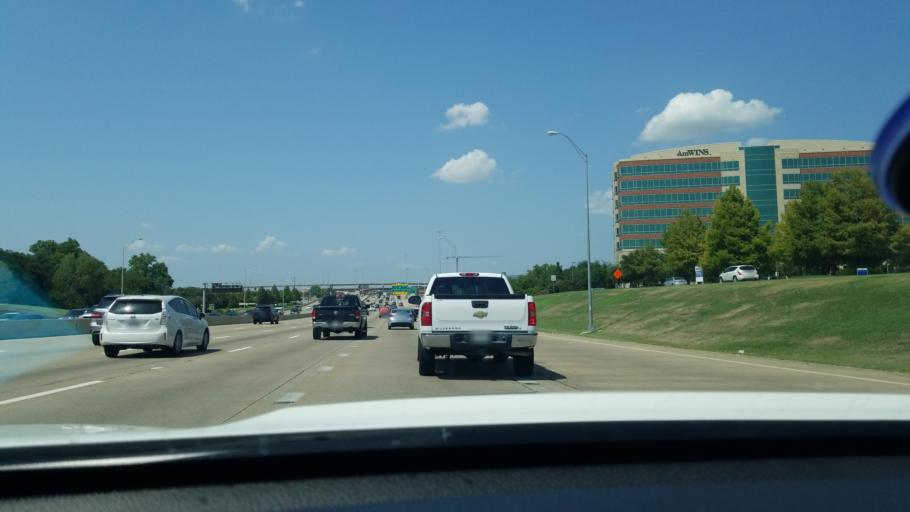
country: US
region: Texas
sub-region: Collin County
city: Plano
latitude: 32.9914
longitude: -96.7098
